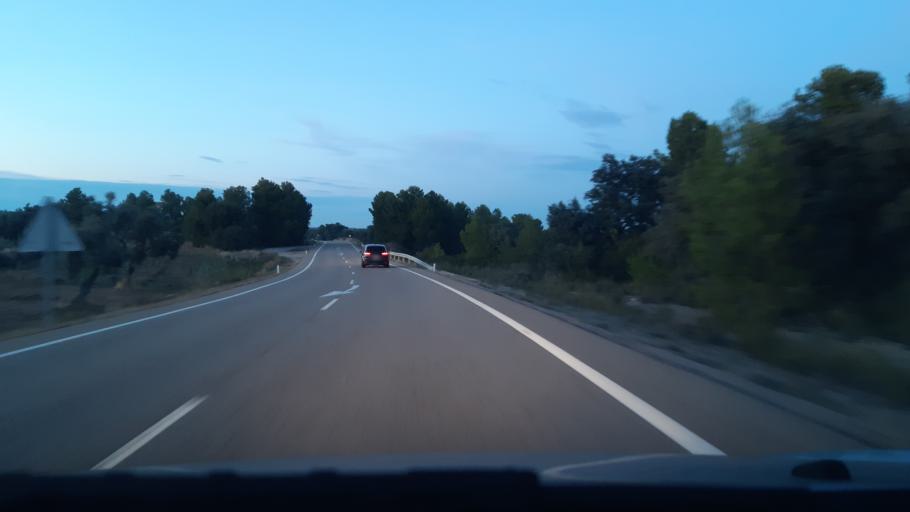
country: ES
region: Aragon
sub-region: Provincia de Teruel
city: Calaceite
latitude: 40.9668
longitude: 0.2083
